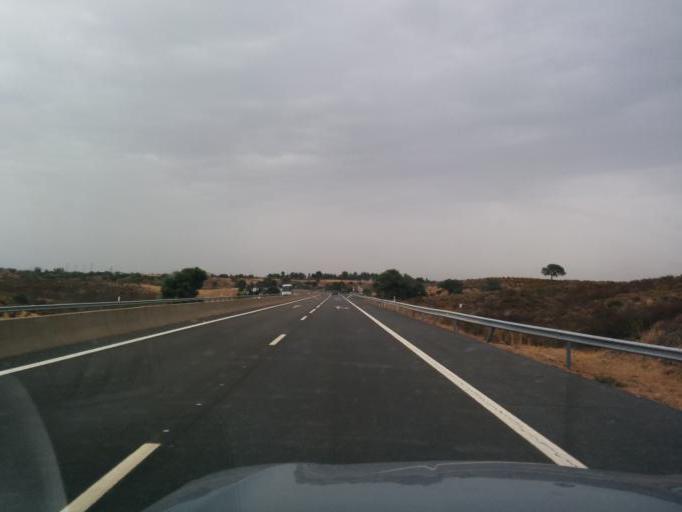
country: PT
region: Faro
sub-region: Tavira
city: Tavira
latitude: 37.1860
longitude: -7.5603
